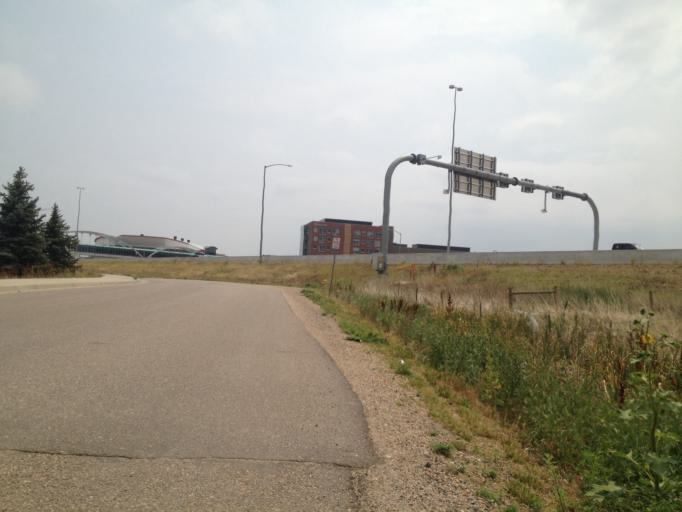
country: US
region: Colorado
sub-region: Broomfield County
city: Broomfield
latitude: 39.9087
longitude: -105.0858
